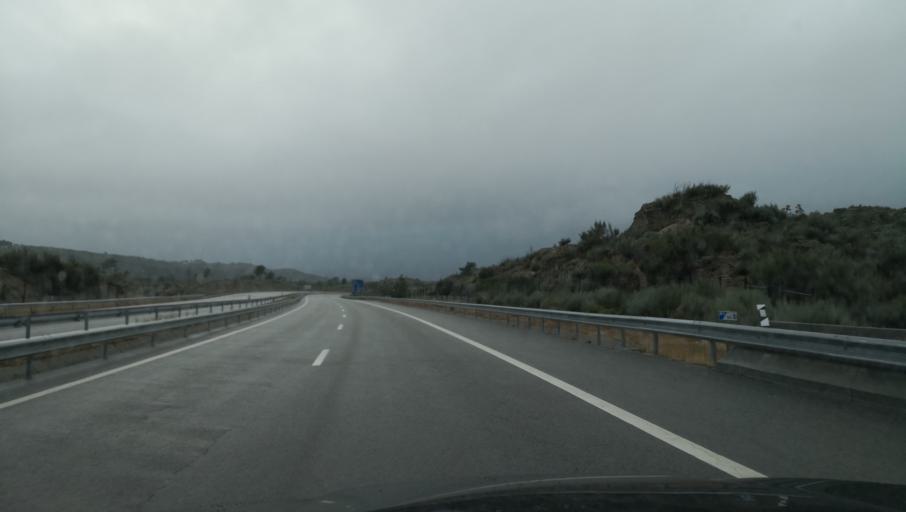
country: PT
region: Vila Real
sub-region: Vila Real
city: Vila Real
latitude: 41.3695
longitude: -7.6815
